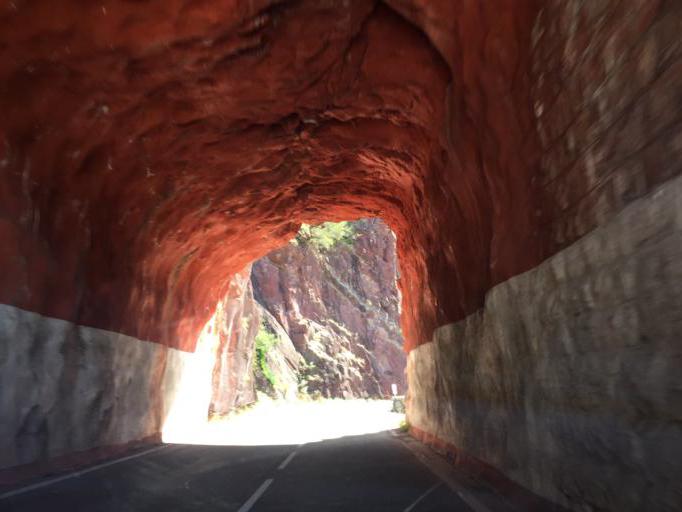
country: FR
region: Provence-Alpes-Cote d'Azur
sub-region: Departement des Alpes-Maritimes
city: Saint-Martin-Vesubie
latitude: 44.0572
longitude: 7.1190
